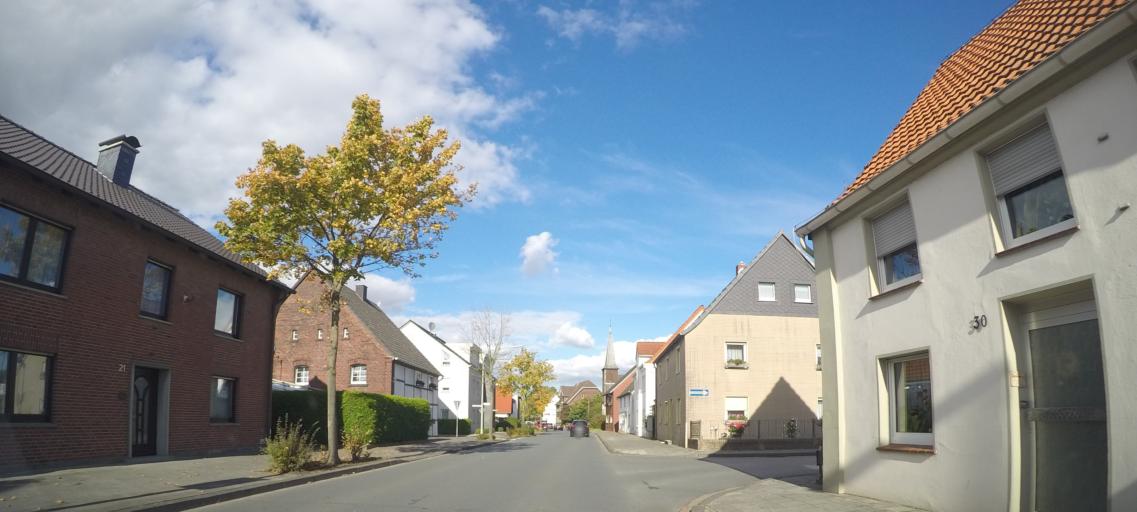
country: DE
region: North Rhine-Westphalia
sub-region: Regierungsbezirk Arnsberg
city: Bad Sassendorf
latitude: 51.6658
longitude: 8.1456
